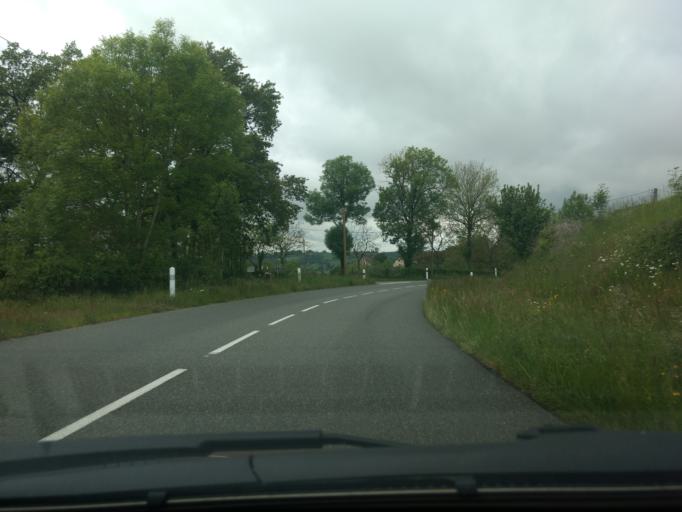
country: FR
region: Midi-Pyrenees
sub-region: Departement de l'Aveyron
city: Viviez
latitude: 44.5462
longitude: 2.1578
